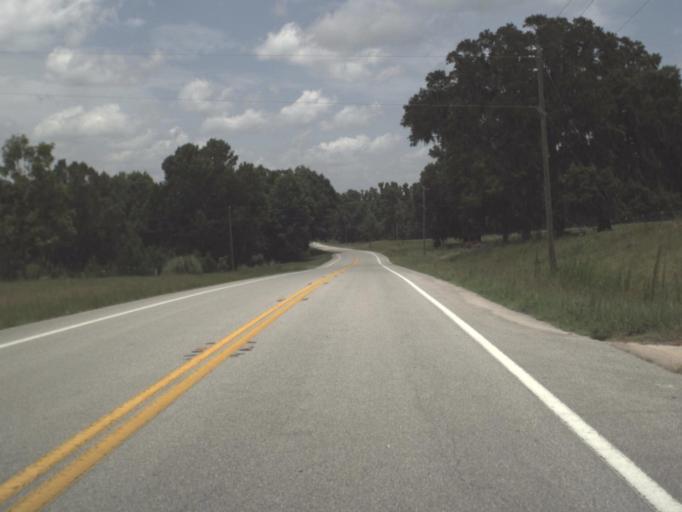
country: US
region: Florida
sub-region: Madison County
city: Madison
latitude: 30.5116
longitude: -83.4228
